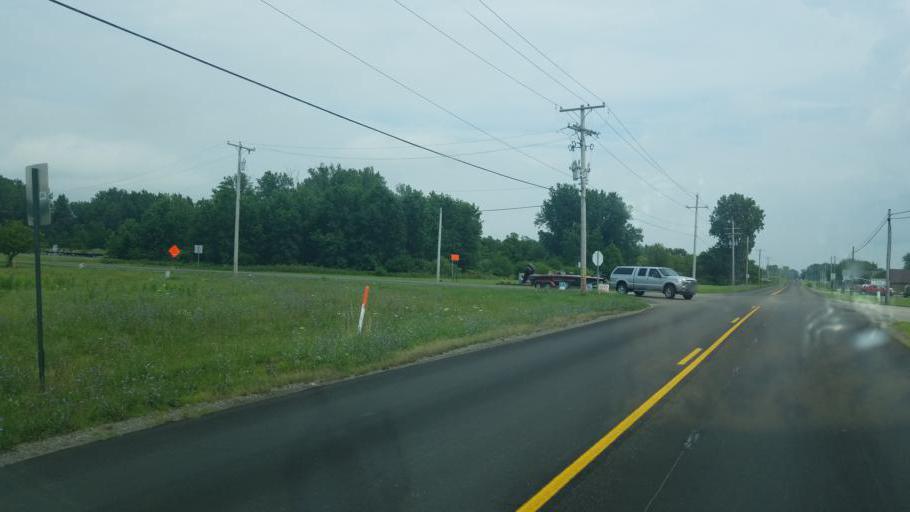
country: US
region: Ohio
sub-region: Logan County
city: Russells Point
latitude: 40.4700
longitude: -83.8568
